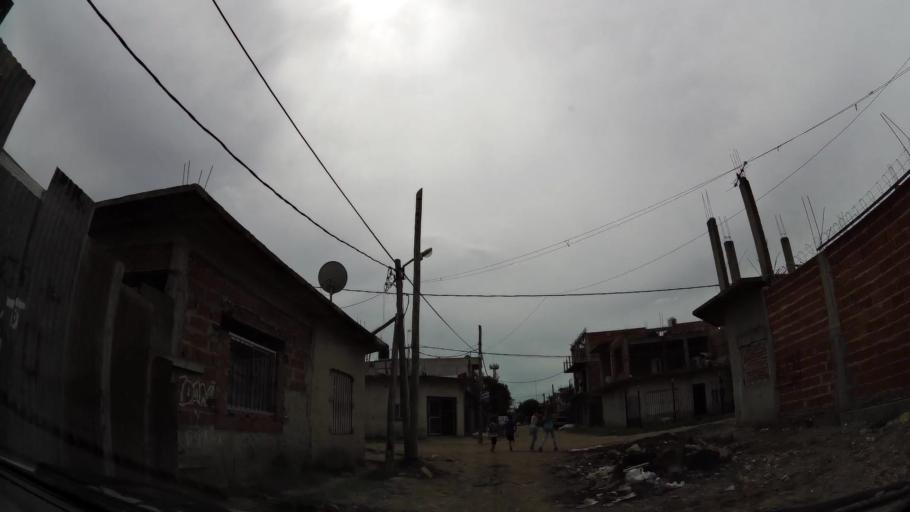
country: AR
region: Buenos Aires
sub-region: Partido de Quilmes
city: Quilmes
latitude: -34.7572
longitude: -58.2553
